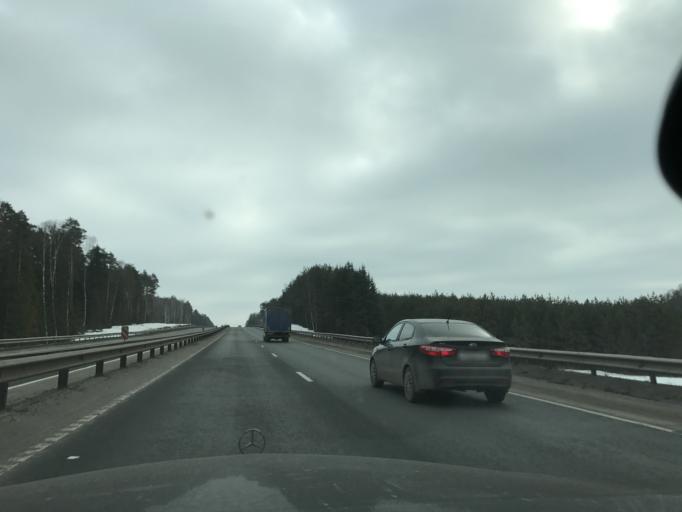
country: RU
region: Vladimir
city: Stepantsevo
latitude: 56.2316
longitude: 41.7669
